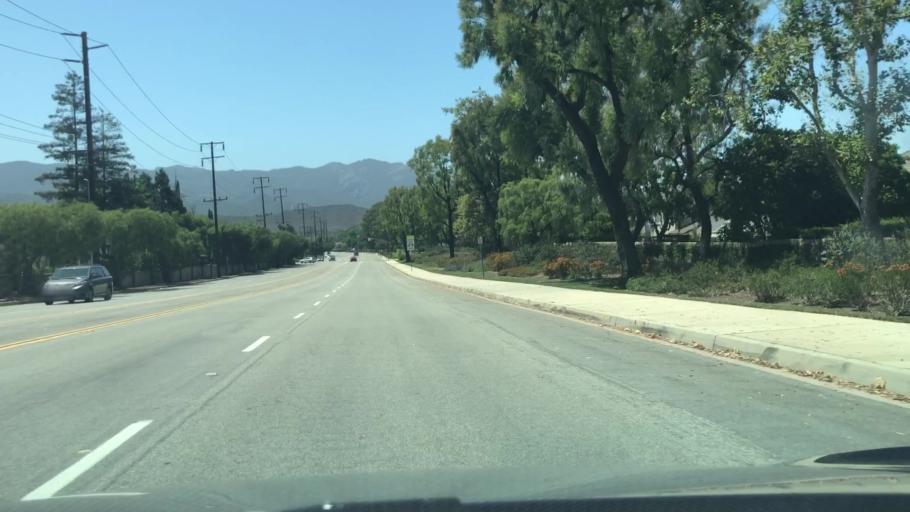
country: US
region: California
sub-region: Ventura County
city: Casa Conejo
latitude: 34.1884
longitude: -118.9544
